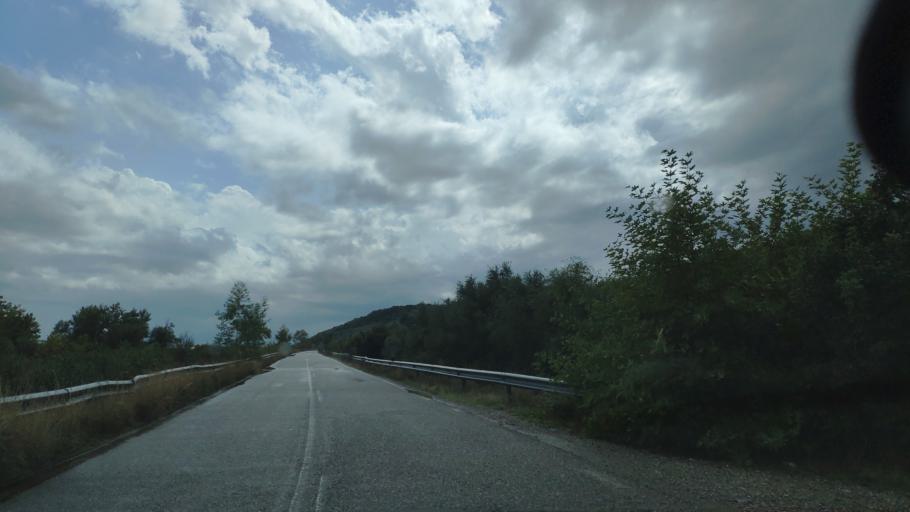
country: GR
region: West Greece
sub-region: Nomos Aitolias kai Akarnanias
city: Lepenou
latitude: 38.6965
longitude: 21.3200
